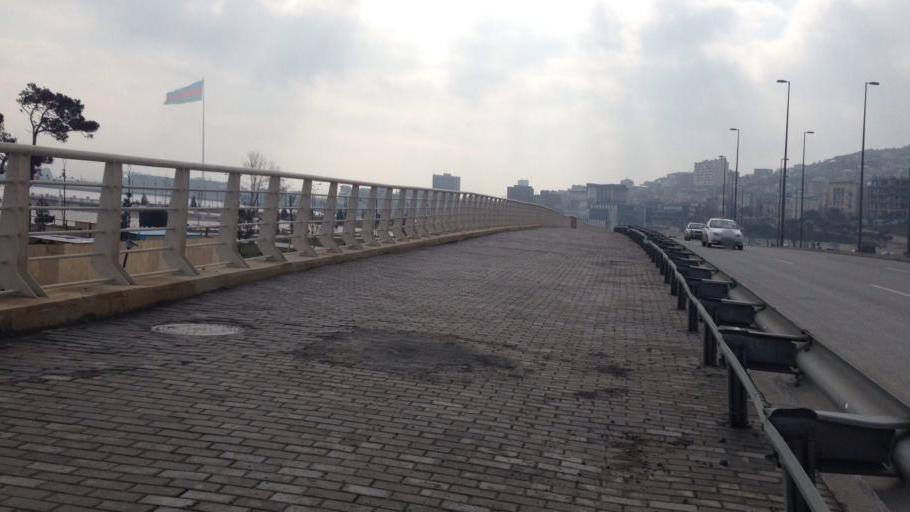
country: AZ
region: Baki
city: Badamdar
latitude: 40.3561
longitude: 49.8344
